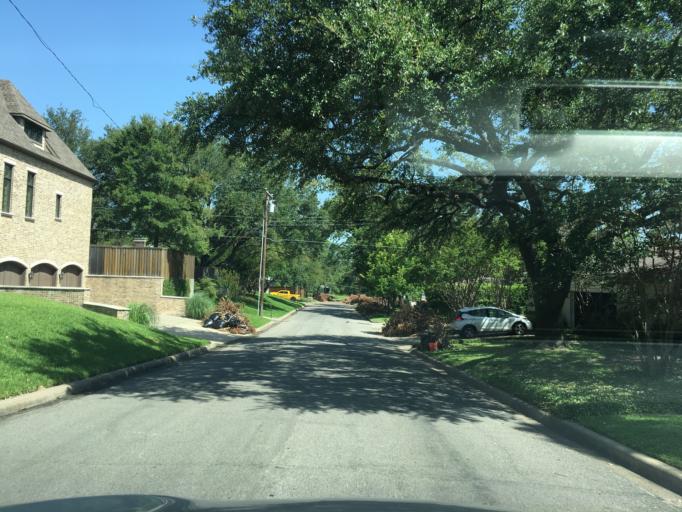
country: US
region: Texas
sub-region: Dallas County
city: University Park
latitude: 32.9046
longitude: -96.7763
